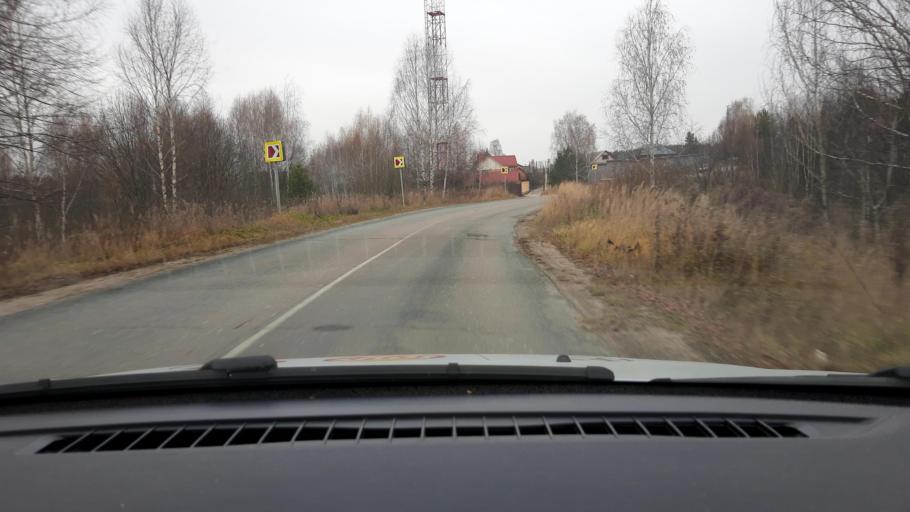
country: RU
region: Nizjnij Novgorod
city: Neklyudovo
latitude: 56.4391
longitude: 43.9129
